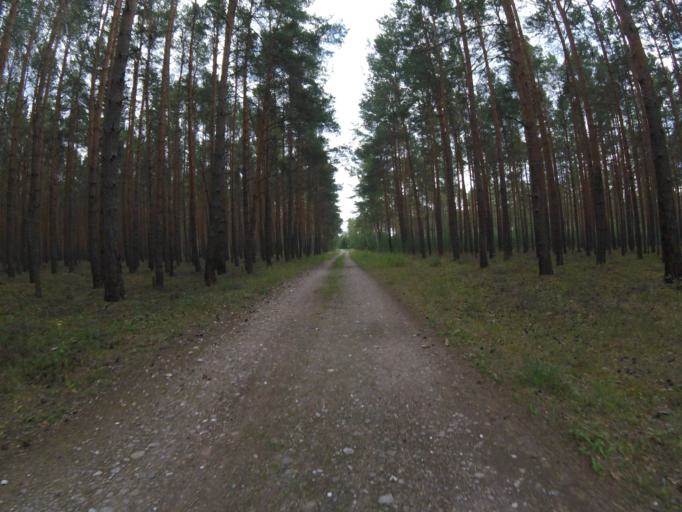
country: DE
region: Brandenburg
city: Halbe
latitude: 52.1191
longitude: 13.6987
